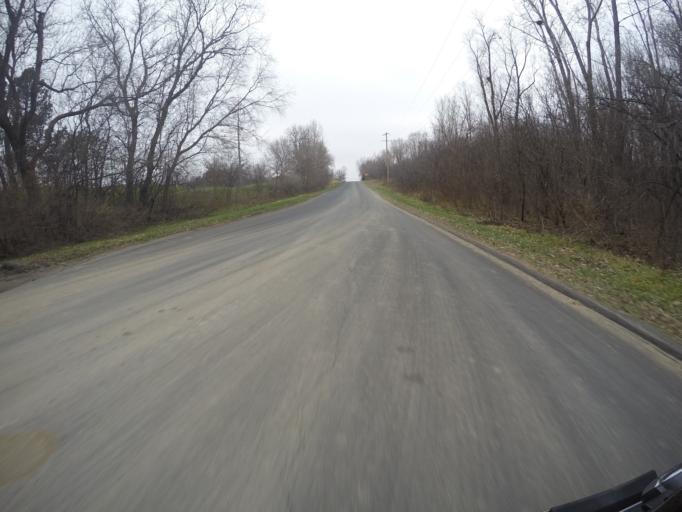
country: US
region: Minnesota
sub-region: Hennepin County
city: Eden Prairie
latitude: 44.8890
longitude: -93.4612
